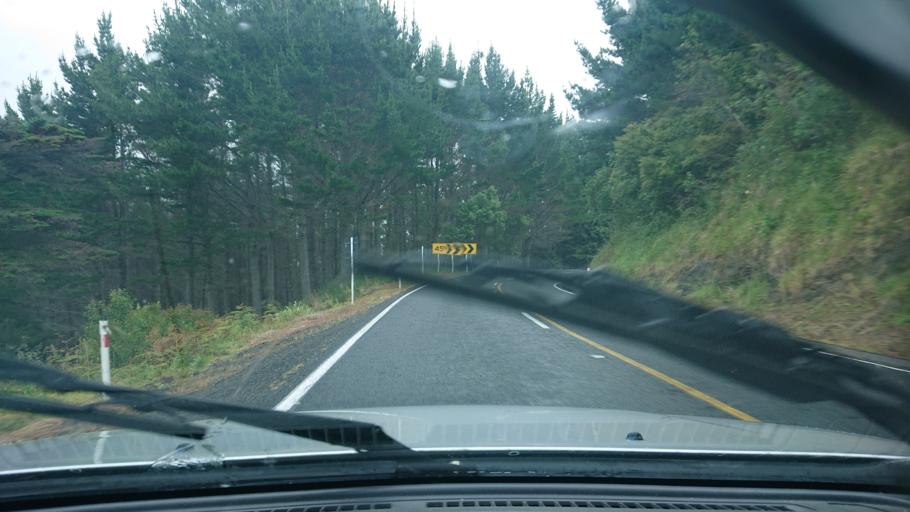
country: NZ
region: Auckland
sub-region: Auckland
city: Wellsford
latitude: -36.3595
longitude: 174.4675
